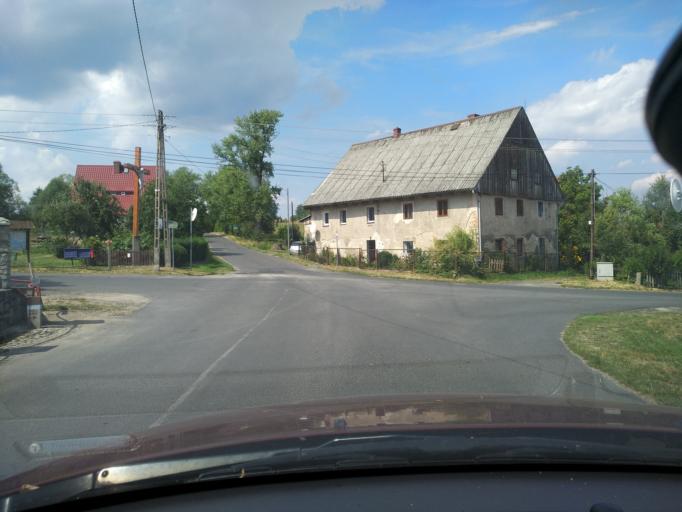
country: PL
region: Lower Silesian Voivodeship
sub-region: Powiat jeleniogorski
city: Stara Kamienica
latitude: 50.8868
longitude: 15.5488
